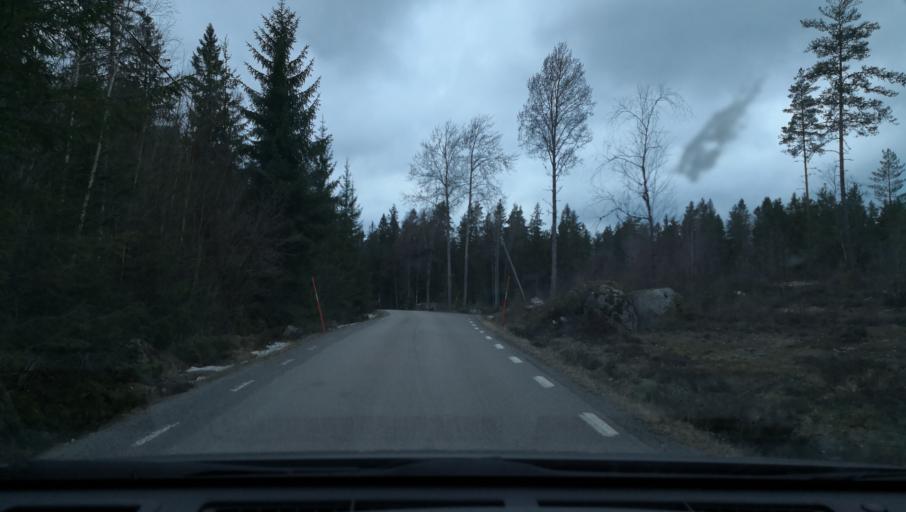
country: SE
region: Vaestmanland
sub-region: Kopings Kommun
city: Kolsva
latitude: 59.5731
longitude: 15.7175
